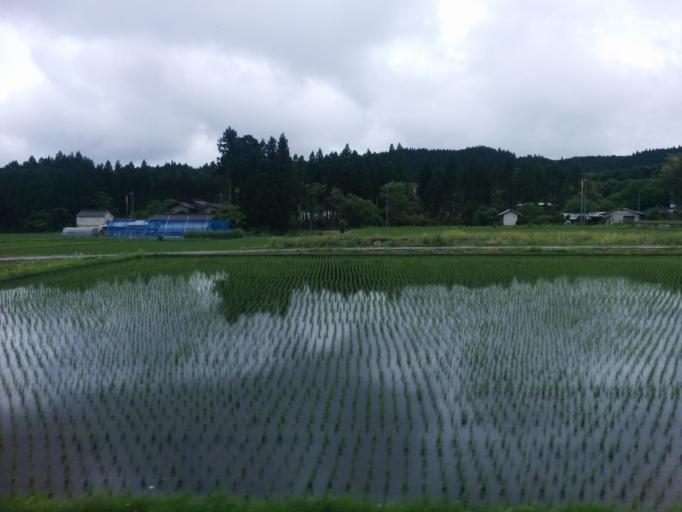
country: JP
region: Tochigi
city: Imaichi
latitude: 36.7291
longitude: 139.6634
